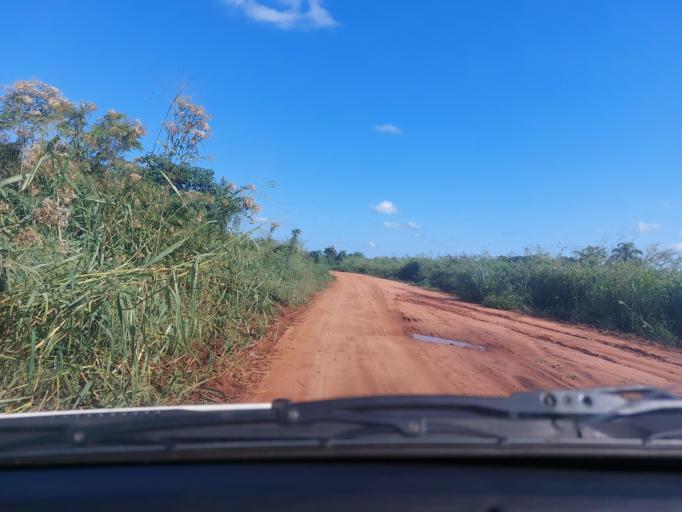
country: PY
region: San Pedro
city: Guayaybi
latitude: -24.5215
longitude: -56.5463
